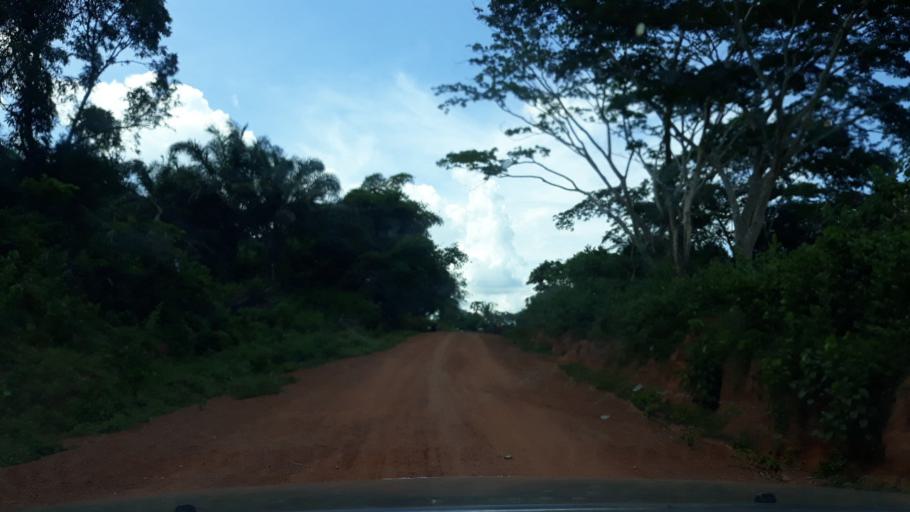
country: CD
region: Equateur
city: Businga
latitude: 3.4016
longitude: 20.3802
